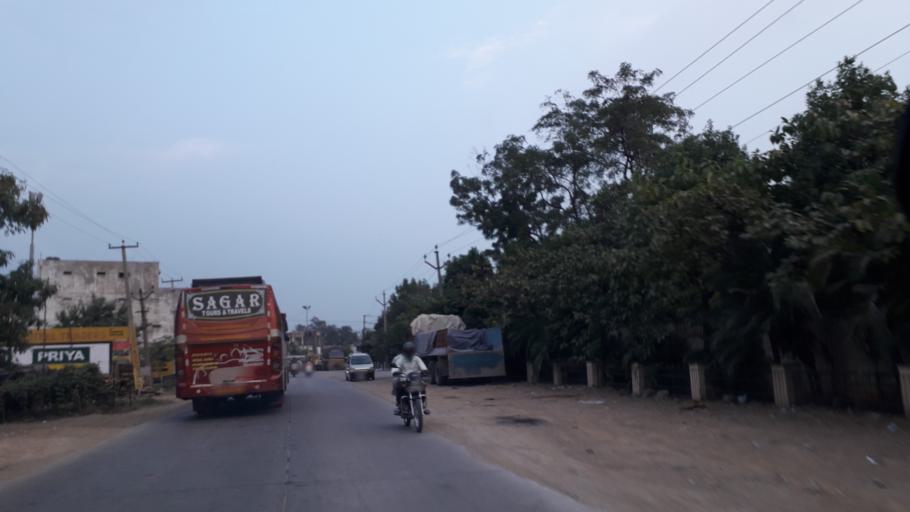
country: IN
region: Telangana
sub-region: Medak
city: Patancheru
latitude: 17.5238
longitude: 78.2472
